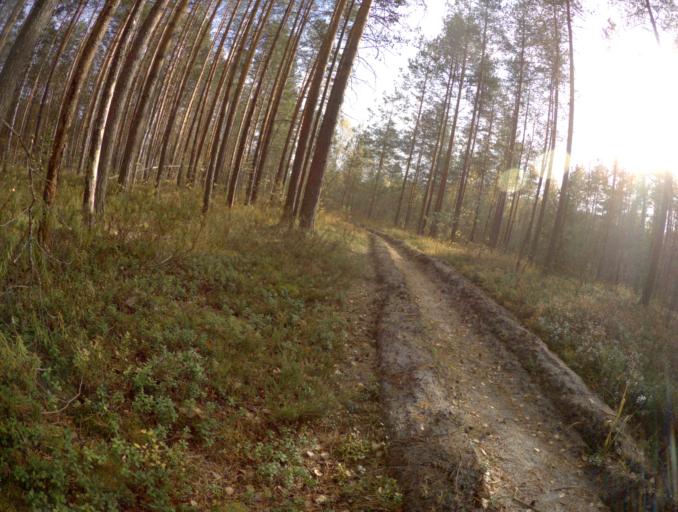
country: RU
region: Vladimir
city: Raduzhnyy
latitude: 55.9391
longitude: 40.3278
